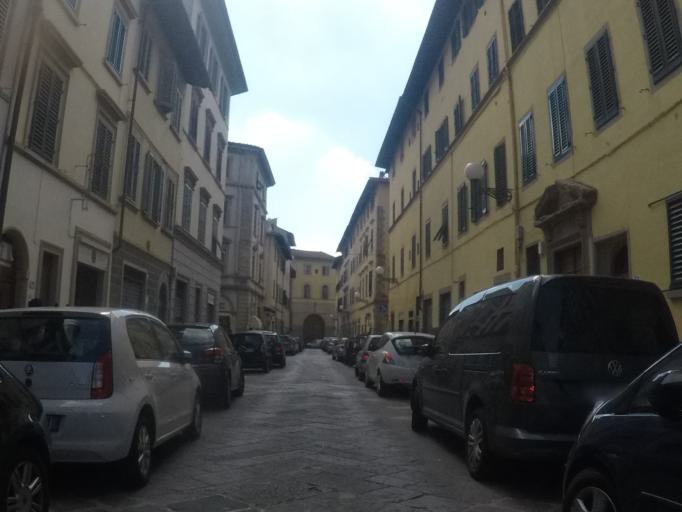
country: IT
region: Tuscany
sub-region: Province of Florence
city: Florence
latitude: 43.7806
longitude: 11.2574
